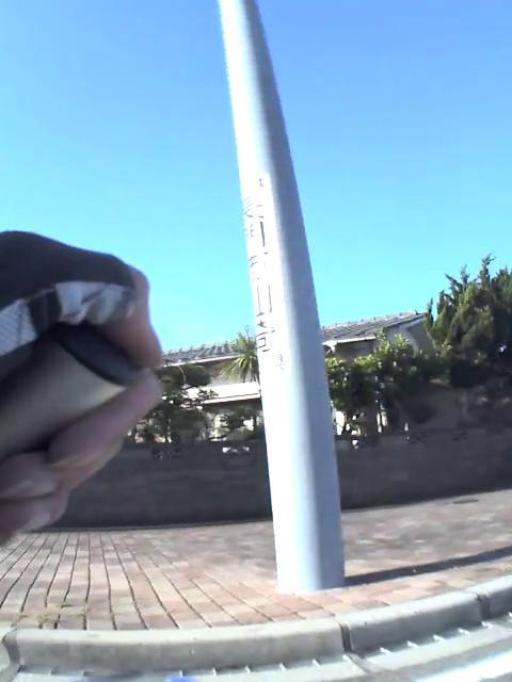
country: JP
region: Yamaguchi
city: Nagato
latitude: 34.3879
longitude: 131.1945
